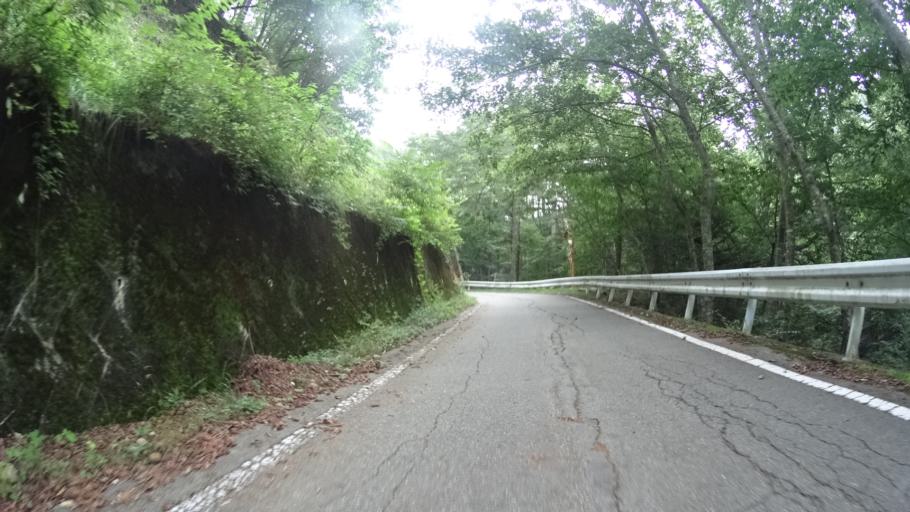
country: JP
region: Yamanashi
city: Kofu-shi
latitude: 35.8569
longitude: 138.5706
